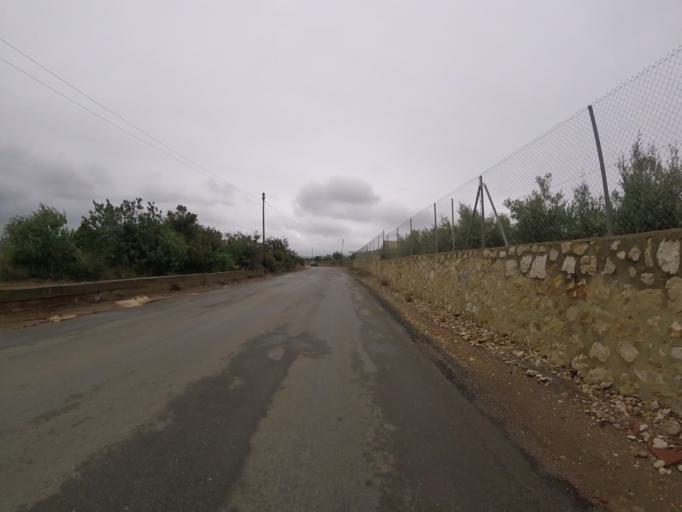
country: ES
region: Valencia
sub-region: Provincia de Castello
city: Alcoceber
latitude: 40.2416
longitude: 0.2492
